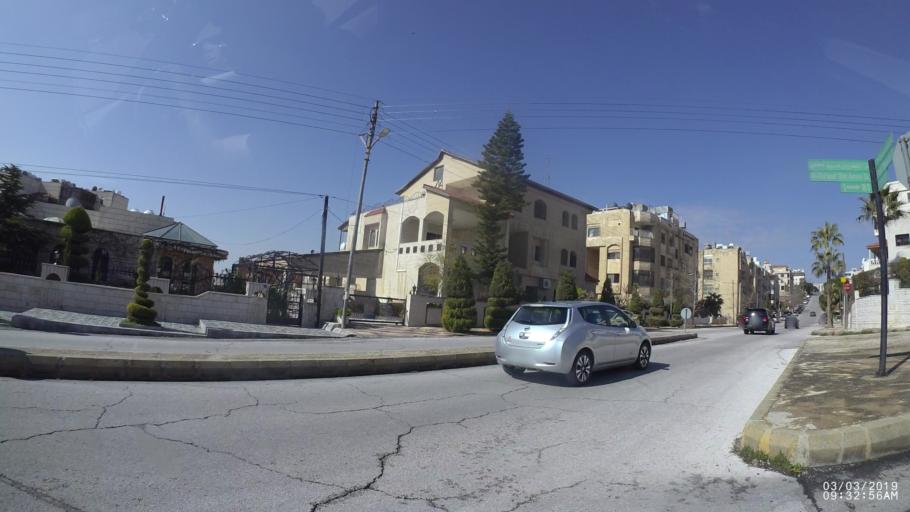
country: JO
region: Amman
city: Al Jubayhah
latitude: 31.9970
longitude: 35.8927
